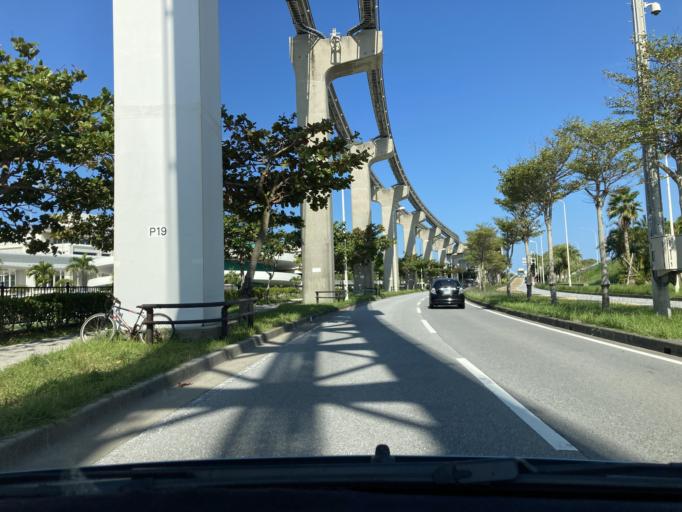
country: JP
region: Okinawa
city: Naha-shi
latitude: 26.2041
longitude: 127.6525
